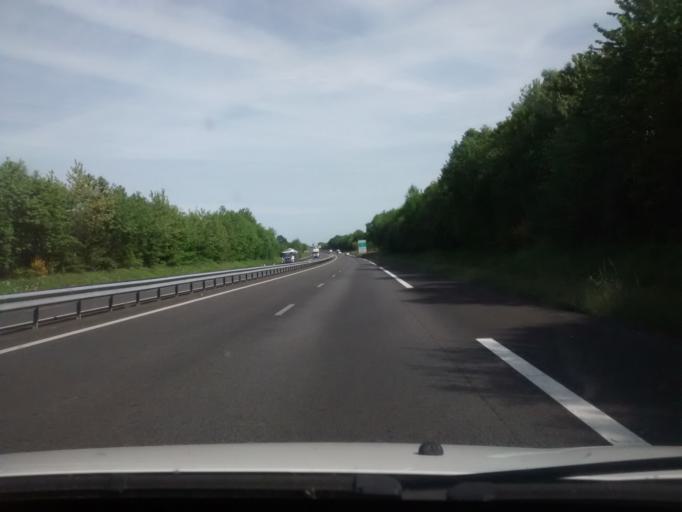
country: FR
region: Brittany
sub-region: Departement d'Ille-et-Vilaine
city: Saint-Etienne-en-Cogles
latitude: 48.3822
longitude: -1.3043
